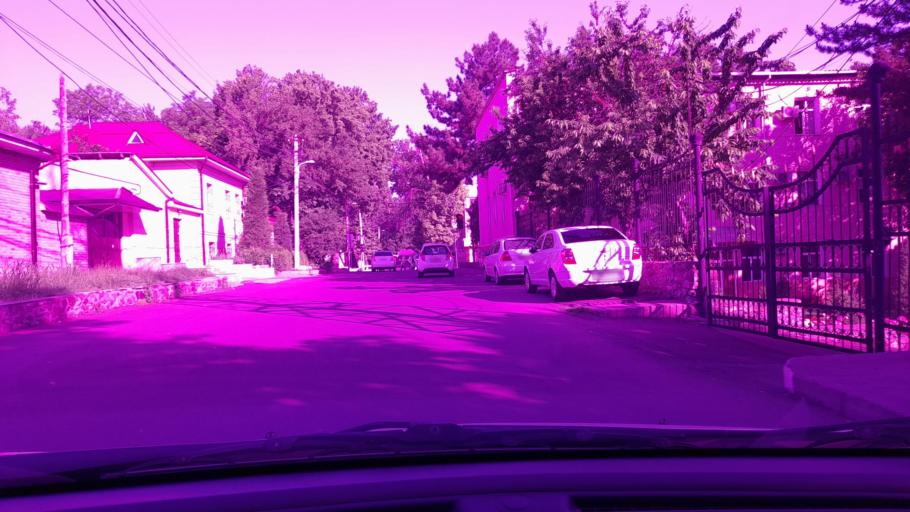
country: UZ
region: Toshkent
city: Salor
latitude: 41.3357
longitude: 69.3550
